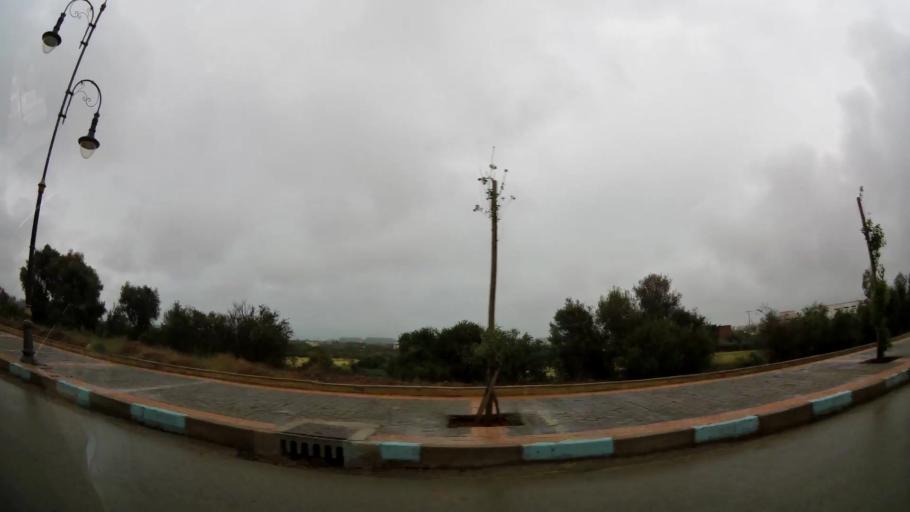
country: MA
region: Taza-Al Hoceima-Taounate
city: Imzourene
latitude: 35.1756
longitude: -3.8742
